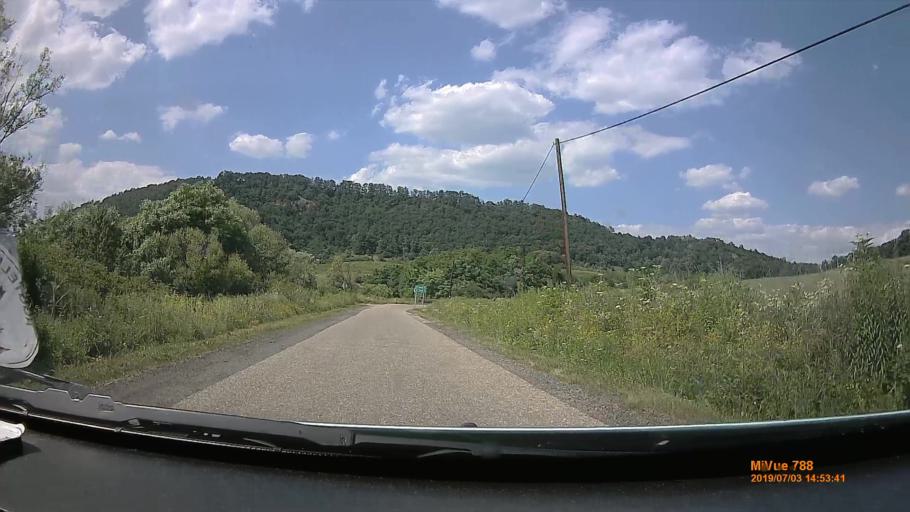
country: HU
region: Borsod-Abauj-Zemplen
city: Putnok
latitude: 48.2598
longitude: 20.4191
